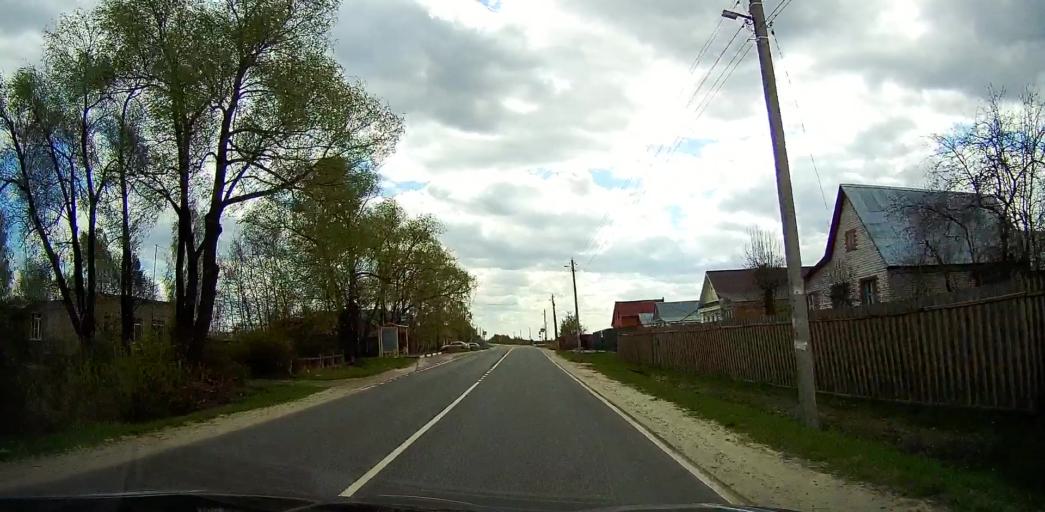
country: RU
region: Moskovskaya
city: Davydovo
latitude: 55.6444
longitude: 38.7507
